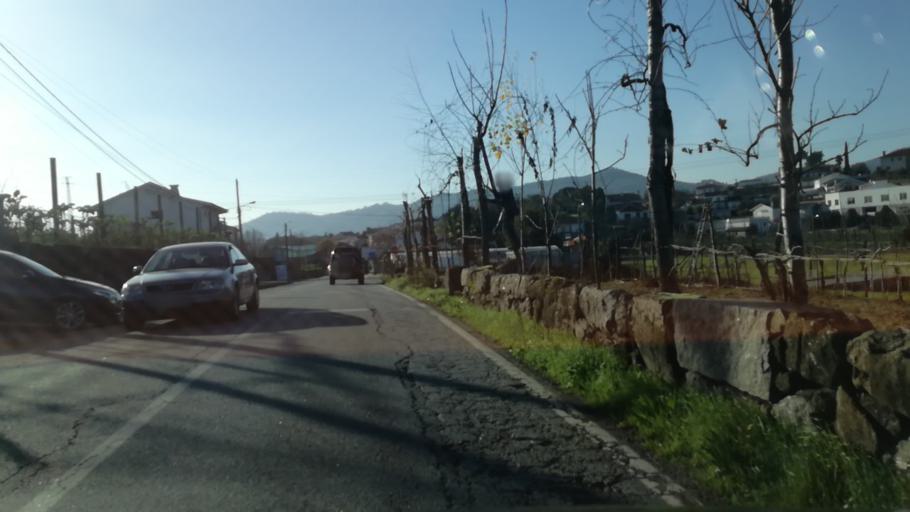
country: PT
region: Braga
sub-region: Guimaraes
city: Ponte
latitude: 41.4994
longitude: -8.3300
